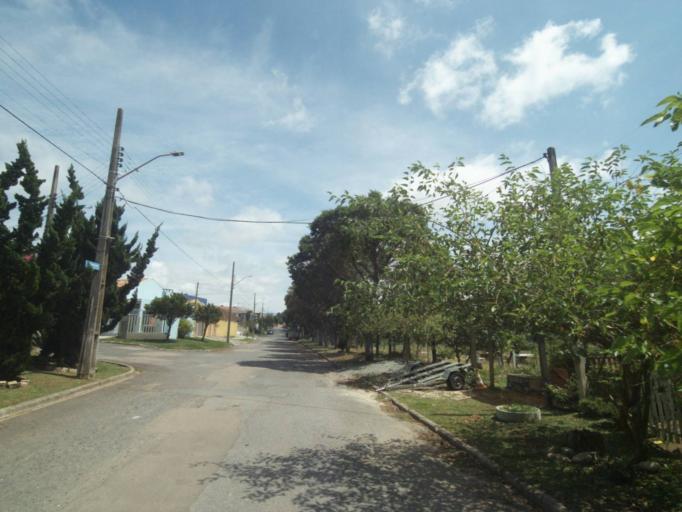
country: BR
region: Parana
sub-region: Curitiba
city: Curitiba
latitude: -25.4581
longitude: -49.3557
